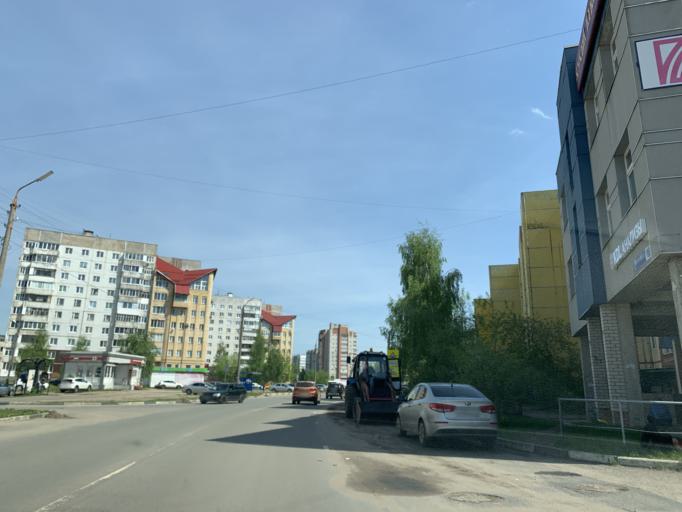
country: RU
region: Jaroslavl
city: Yaroslavl
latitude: 57.6516
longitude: 39.9529
